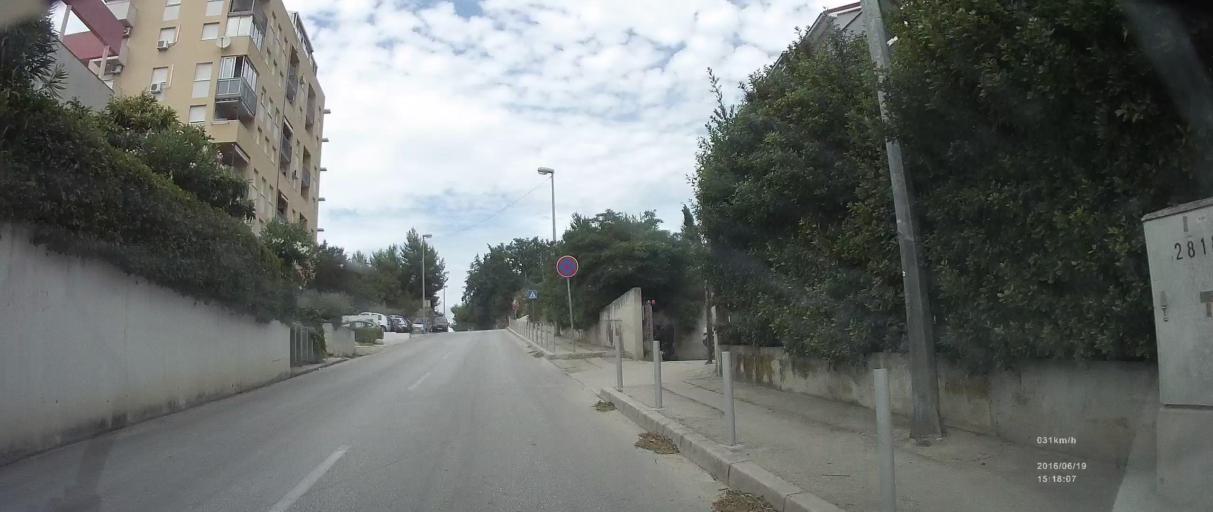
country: HR
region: Splitsko-Dalmatinska
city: Kamen
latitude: 43.5069
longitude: 16.4960
